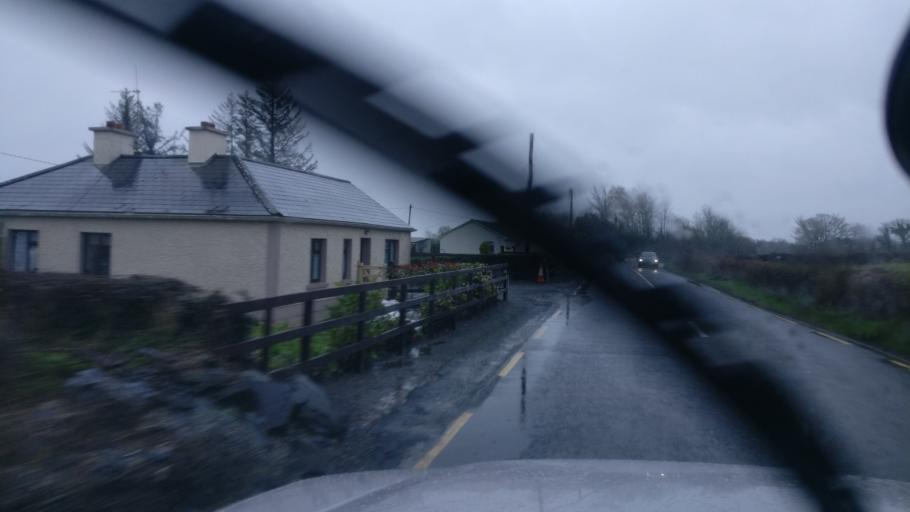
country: IE
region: Connaught
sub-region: County Galway
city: Ballinasloe
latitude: 53.2772
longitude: -8.2105
